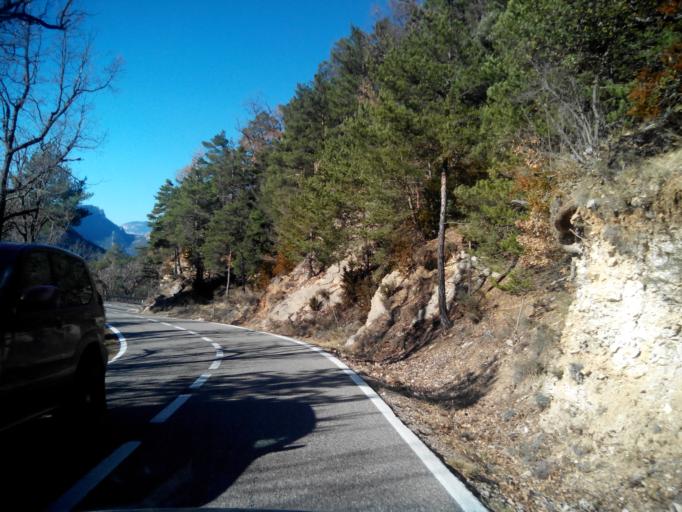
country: ES
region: Catalonia
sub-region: Provincia de Barcelona
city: Capolat
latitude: 42.1007
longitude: 1.7432
